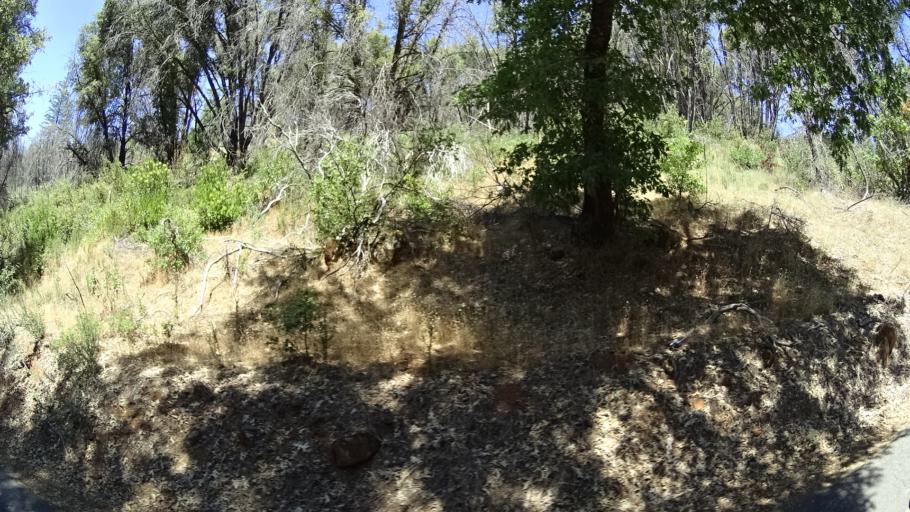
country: US
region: California
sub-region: Calaveras County
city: Mountain Ranch
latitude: 38.2441
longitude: -120.5429
